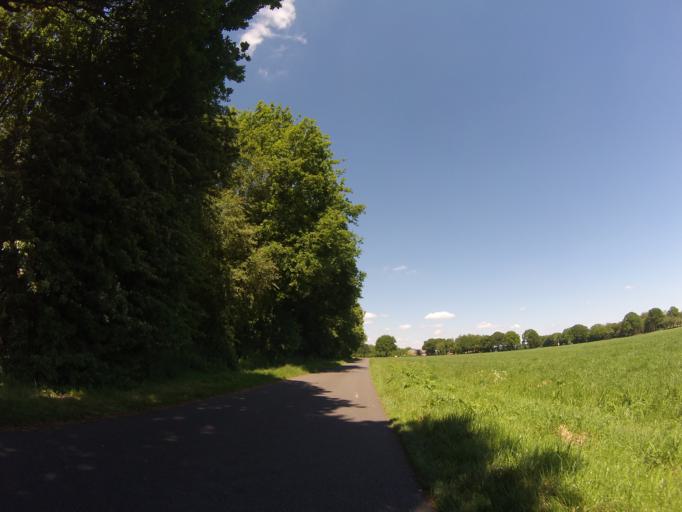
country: NL
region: Drenthe
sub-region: Gemeente Hoogeveen
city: Hoogeveen
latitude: 52.7908
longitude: 6.5320
